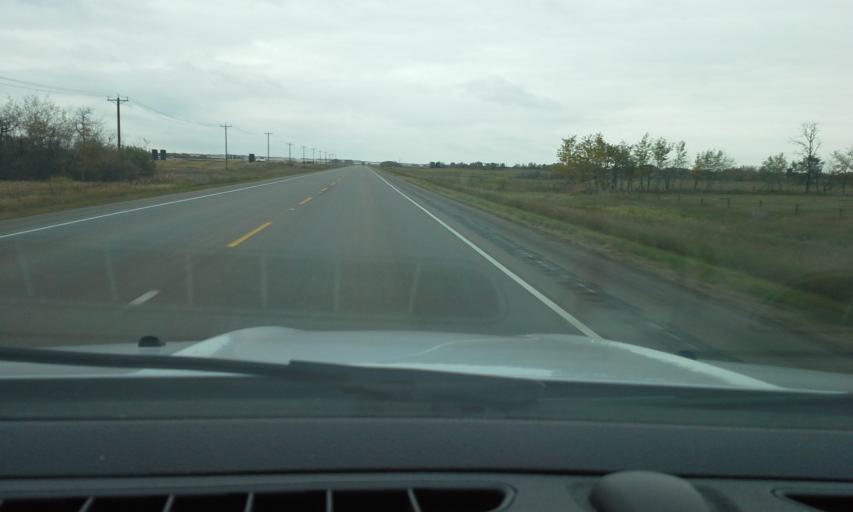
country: CA
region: Saskatchewan
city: Lloydminster
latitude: 53.2780
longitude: -109.8225
